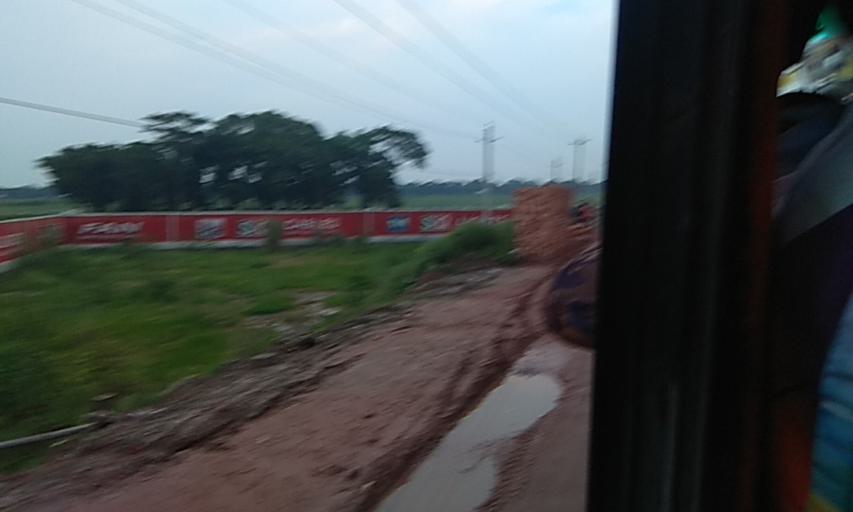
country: BD
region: Dhaka
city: Char Bhadrasan
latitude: 23.3847
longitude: 89.9969
